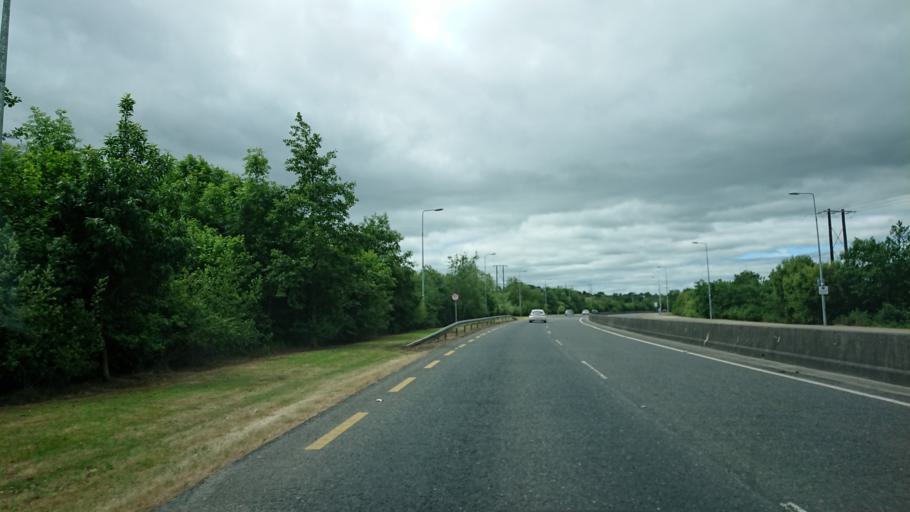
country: IE
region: Munster
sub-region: Waterford
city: Waterford
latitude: 52.2255
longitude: -7.1199
